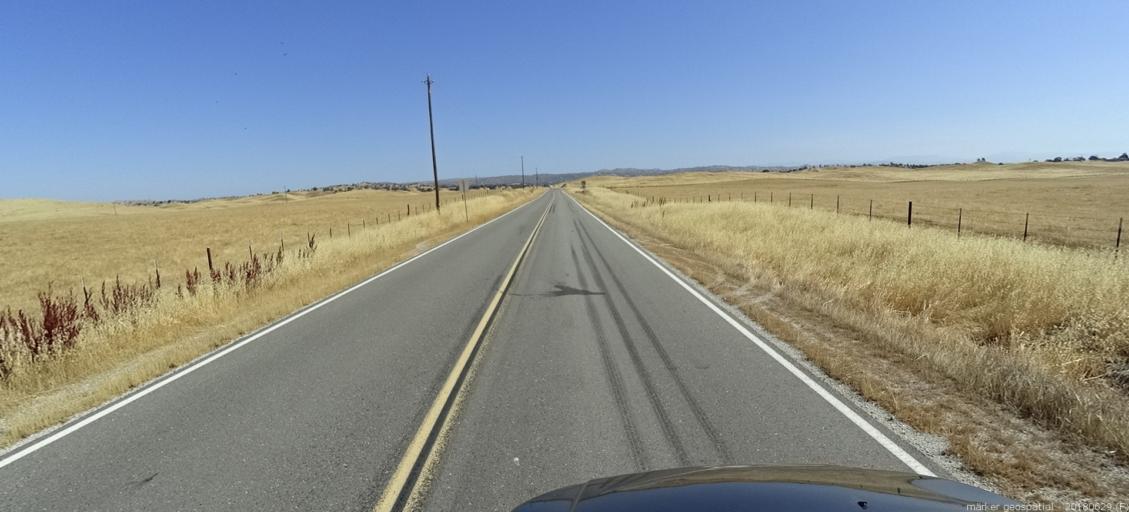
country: US
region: California
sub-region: Madera County
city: Bonadelle Ranchos-Madera Ranchos
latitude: 37.0366
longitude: -119.7937
